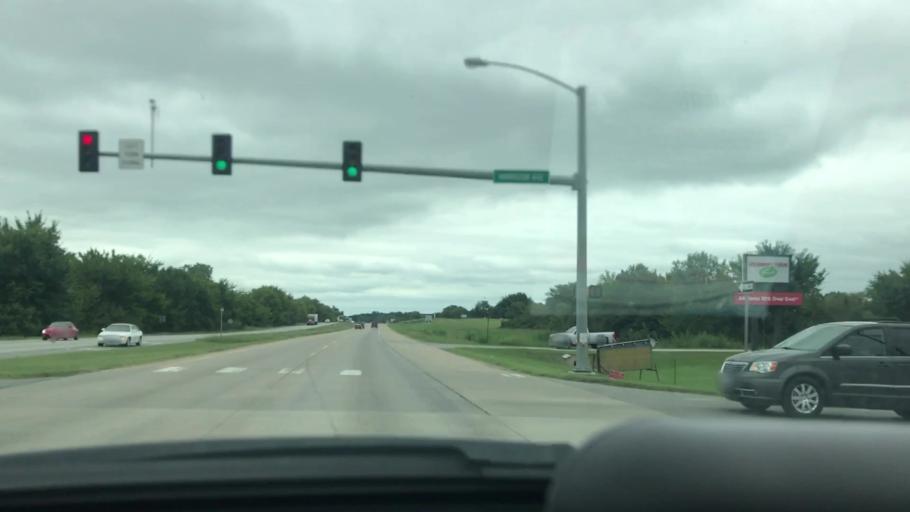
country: US
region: Oklahoma
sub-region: Mayes County
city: Chouteau
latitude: 36.1916
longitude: -95.3420
